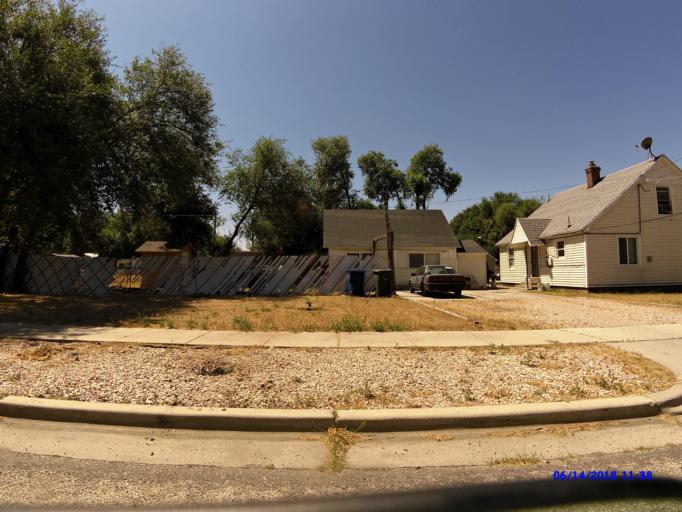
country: US
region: Utah
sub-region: Weber County
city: Ogden
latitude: 41.2209
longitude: -111.9910
